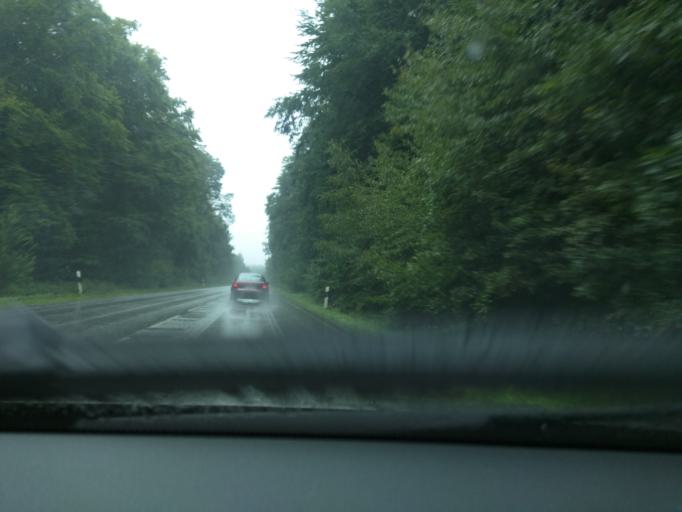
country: DE
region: Schleswig-Holstein
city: Brunstorf
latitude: 53.5172
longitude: 10.4529
